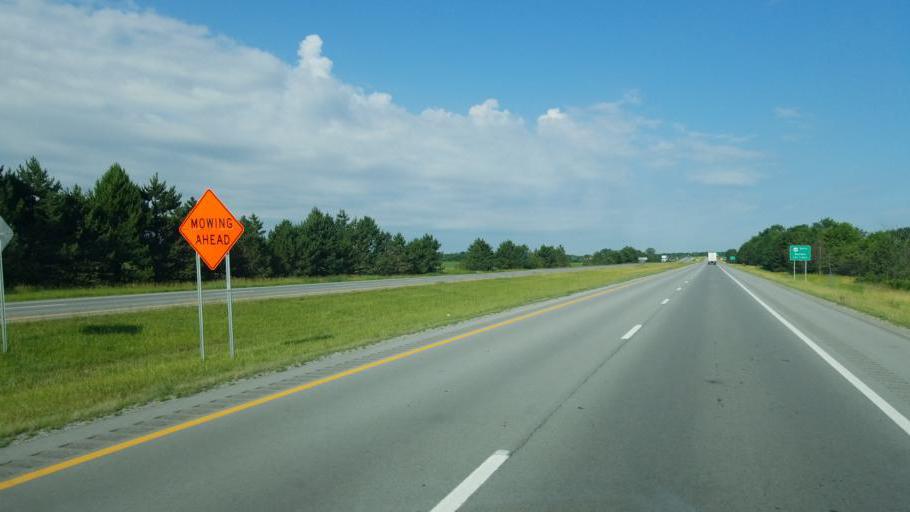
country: US
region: Ohio
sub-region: Hancock County
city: Findlay
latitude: 40.9865
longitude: -83.6278
